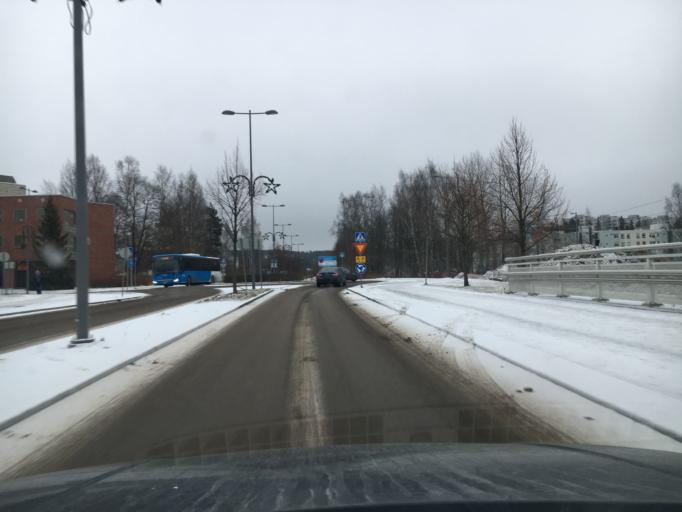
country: FI
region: Uusimaa
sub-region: Helsinki
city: Espoo
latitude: 60.2064
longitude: 24.6608
